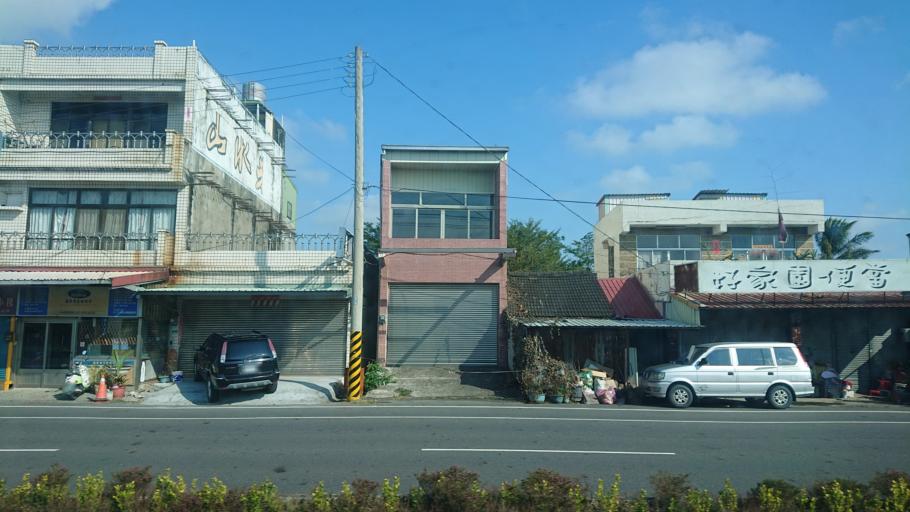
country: TW
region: Taiwan
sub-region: Chiayi
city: Taibao
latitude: 23.4578
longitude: 120.3083
